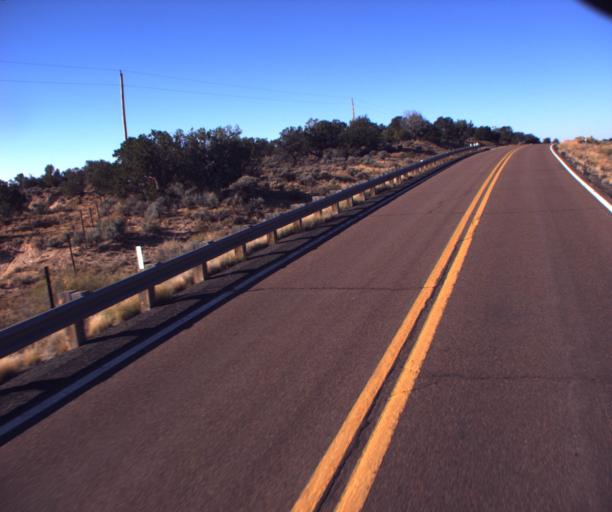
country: US
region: Arizona
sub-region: Apache County
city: Ganado
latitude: 35.7490
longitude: -109.9129
